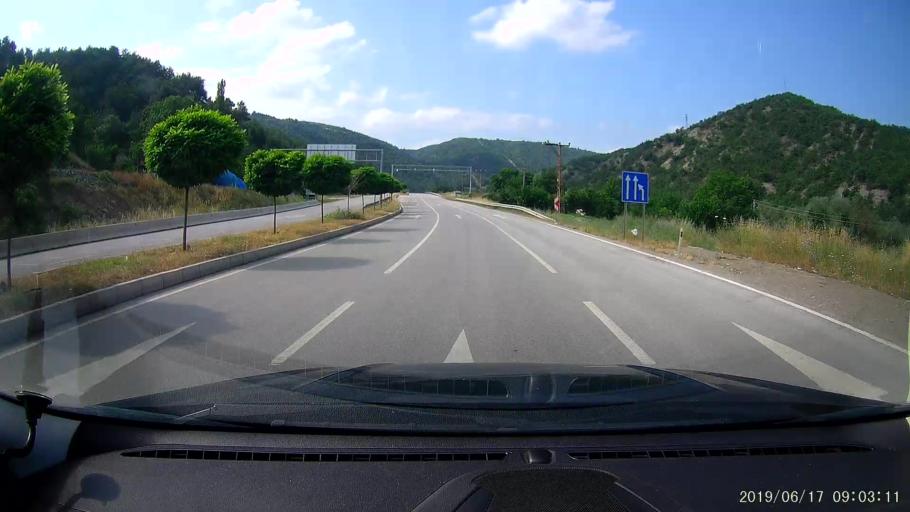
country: TR
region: Amasya
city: Tasova
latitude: 40.7587
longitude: 36.3023
